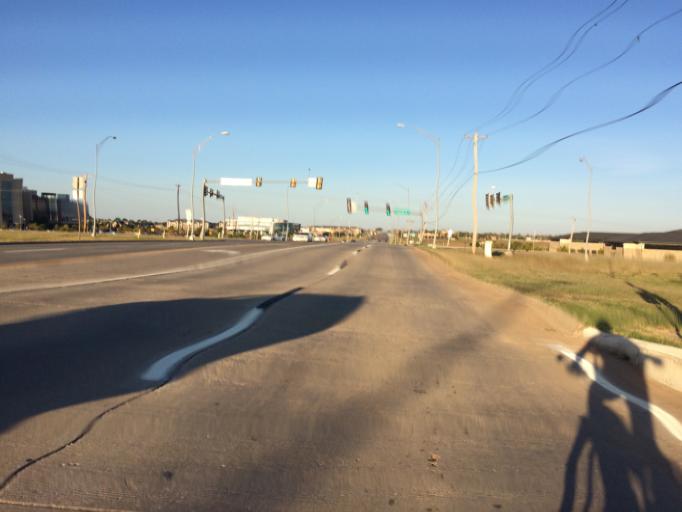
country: US
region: Oklahoma
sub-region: Cleveland County
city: Norman
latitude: 35.2620
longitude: -97.4861
